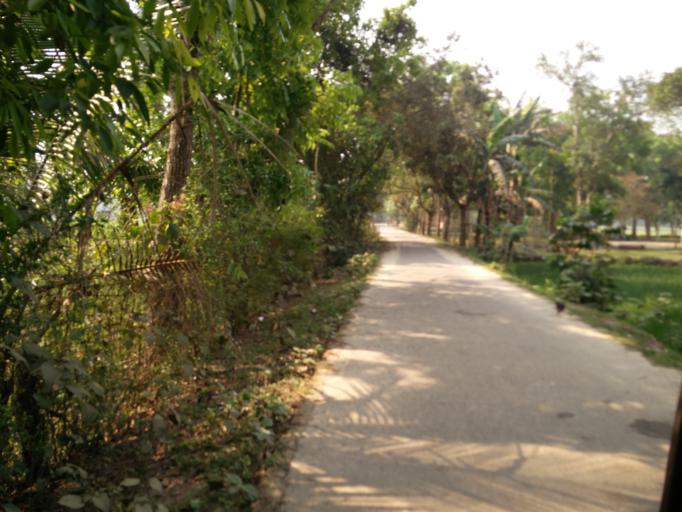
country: BD
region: Dhaka
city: Sherpur
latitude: 24.9172
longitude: 90.1574
